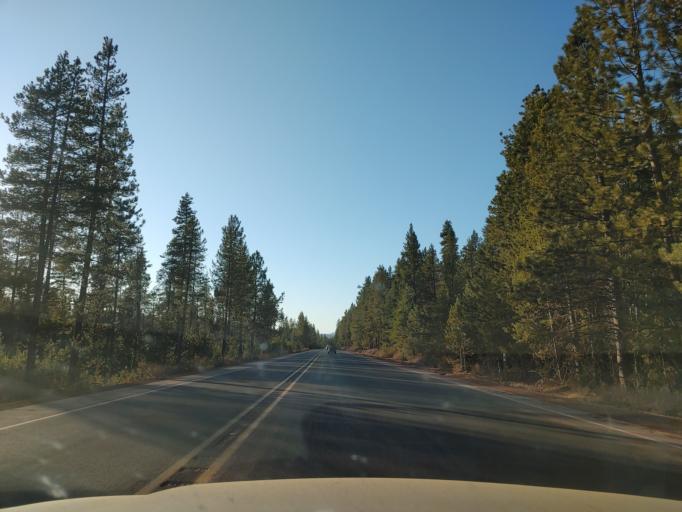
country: US
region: Oregon
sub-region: Deschutes County
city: La Pine
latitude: 43.4576
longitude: -121.8783
